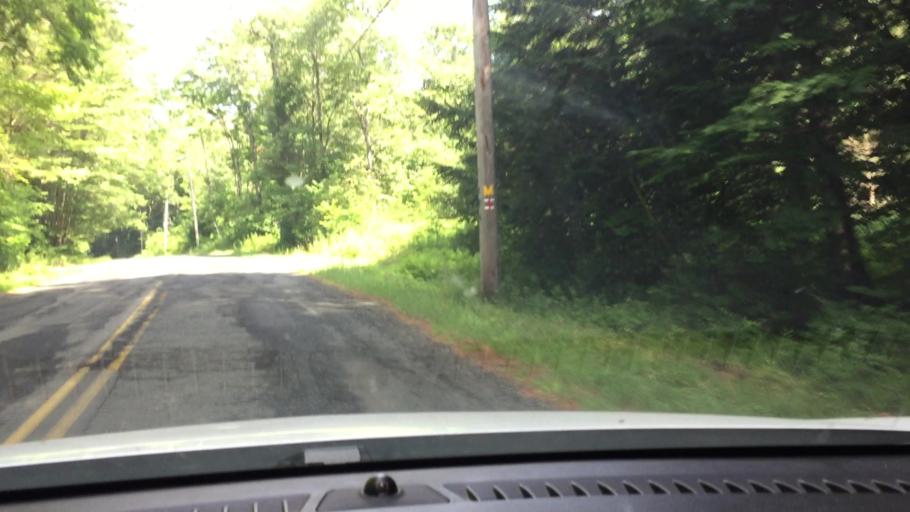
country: US
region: Massachusetts
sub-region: Berkshire County
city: Otis
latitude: 42.1872
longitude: -73.1507
